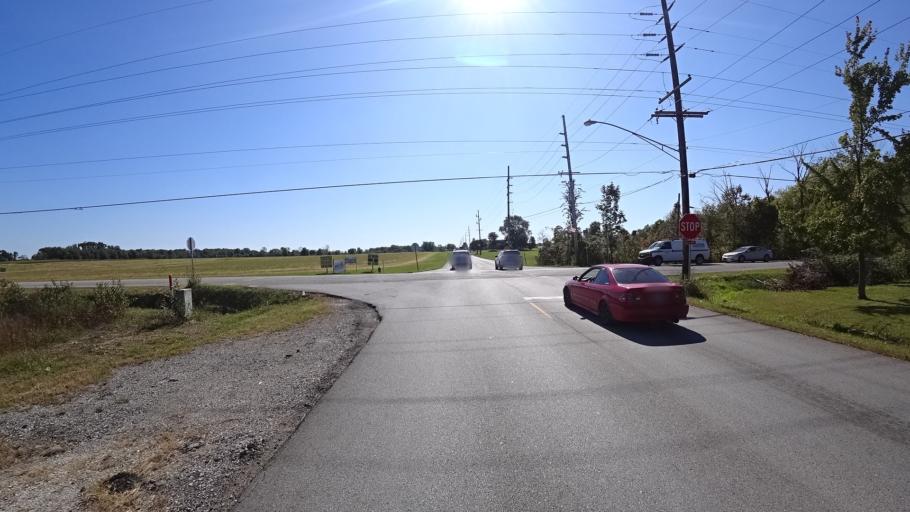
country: US
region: Indiana
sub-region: LaPorte County
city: Trail Creek
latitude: 41.6804
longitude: -86.8745
